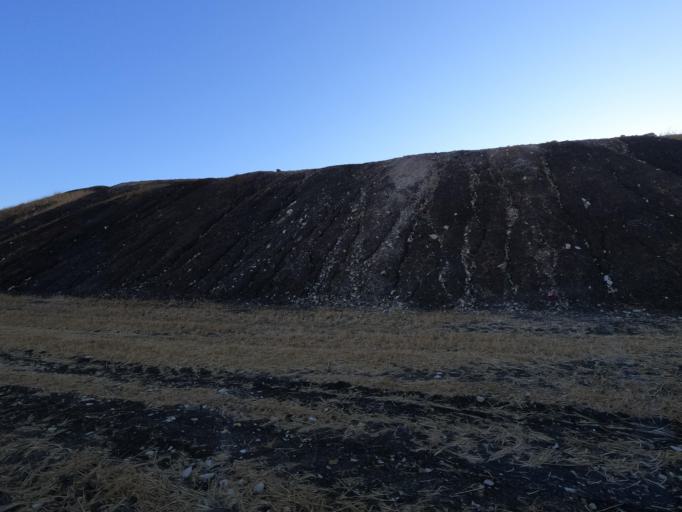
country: CY
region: Larnaka
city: Troulloi
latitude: 35.0287
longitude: 33.6398
